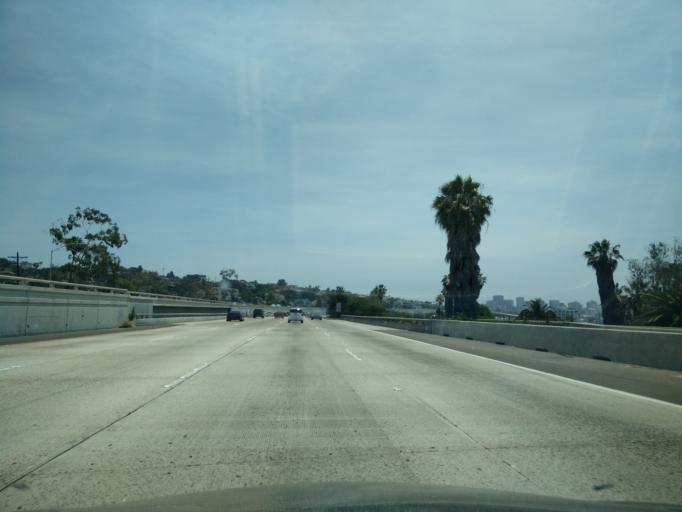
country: US
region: California
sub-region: San Diego County
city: San Diego
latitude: 32.7428
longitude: -117.1835
